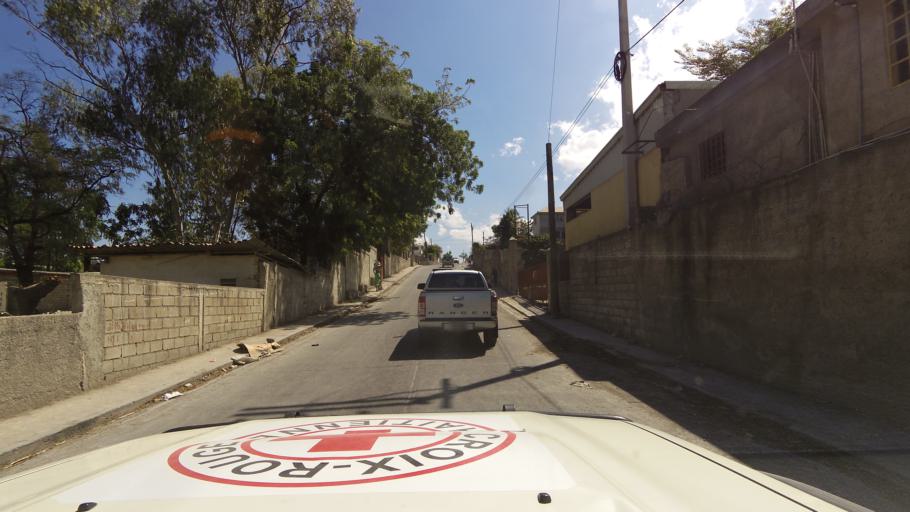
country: HT
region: Ouest
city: Delmas 73
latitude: 18.5715
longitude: -72.3013
